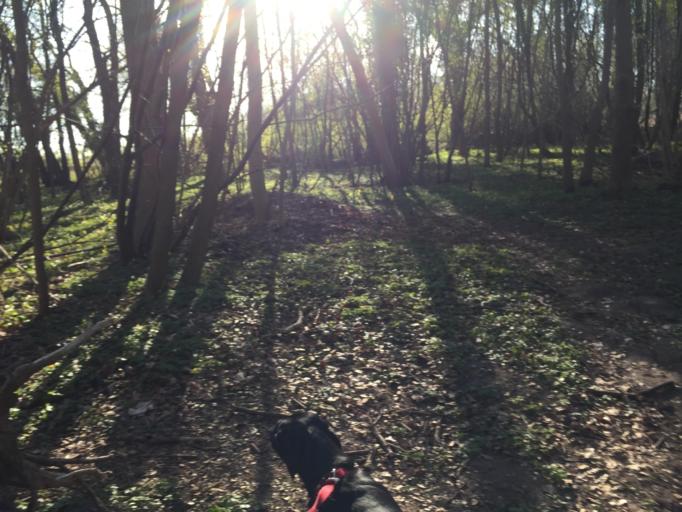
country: DK
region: South Denmark
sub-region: Odense Kommune
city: Neder Holluf
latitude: 55.3717
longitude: 10.4202
